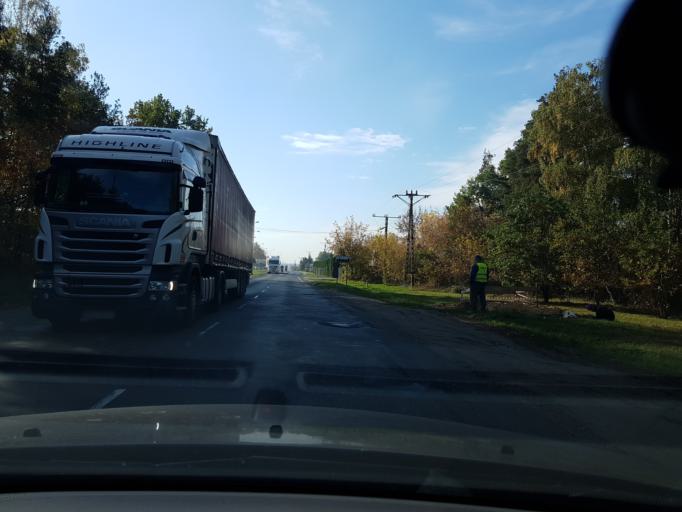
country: PL
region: Lodz Voivodeship
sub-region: Powiat tomaszowski
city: Tomaszow Mazowiecki
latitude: 51.5610
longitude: 20.0210
